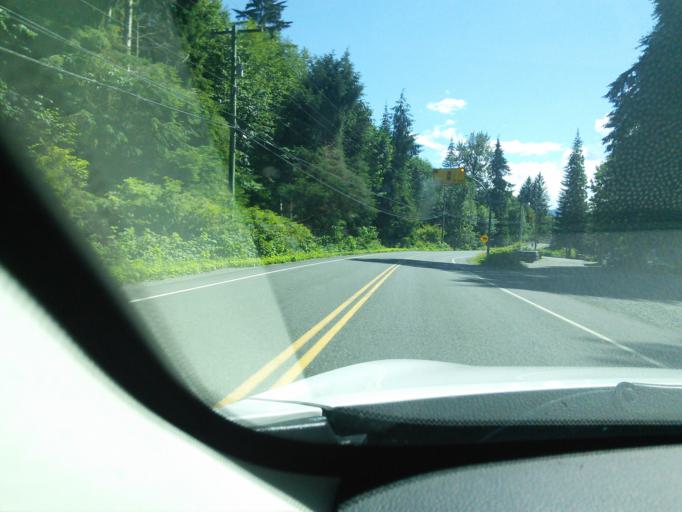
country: CA
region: British Columbia
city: Campbell River
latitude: 50.3225
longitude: -125.9220
